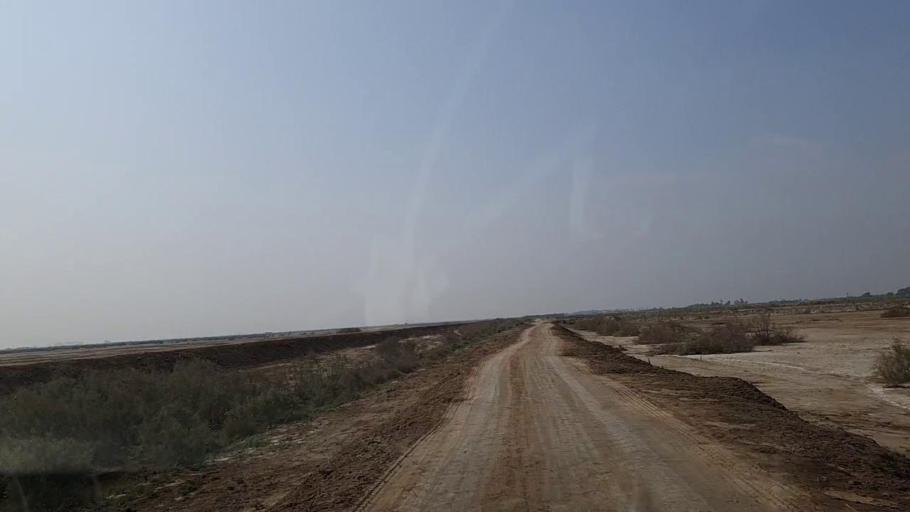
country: PK
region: Sindh
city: Gharo
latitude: 24.6737
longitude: 67.7188
